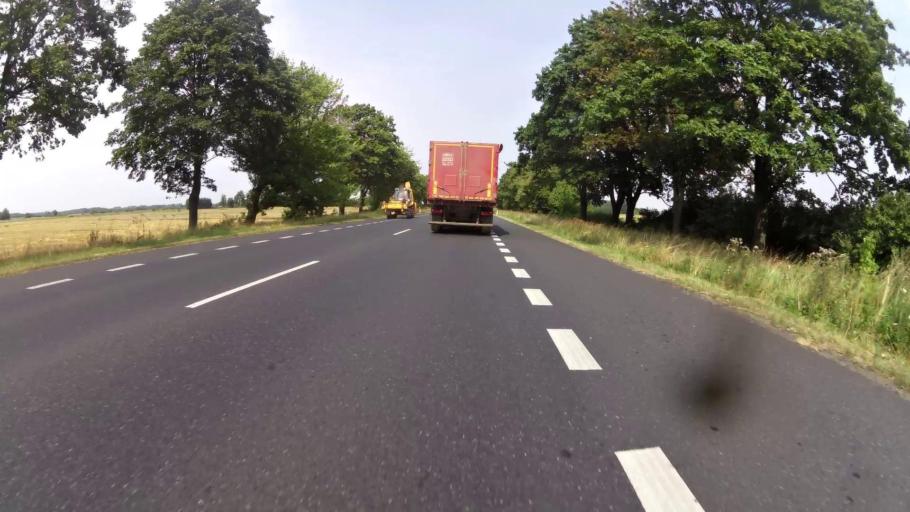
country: PL
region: West Pomeranian Voivodeship
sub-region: Powiat pyrzycki
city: Lipiany
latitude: 52.9652
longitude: 14.9681
